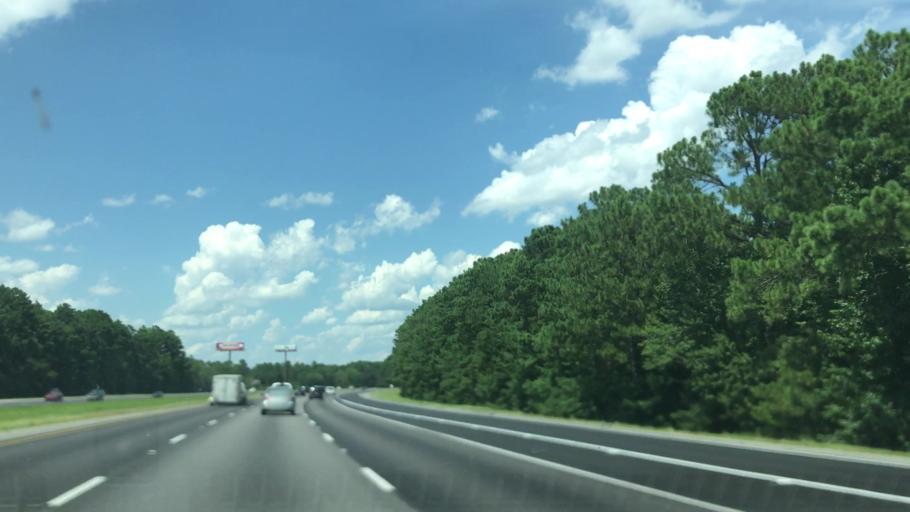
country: US
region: Georgia
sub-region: Chatham County
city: Pooler
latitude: 32.1462
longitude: -81.2404
